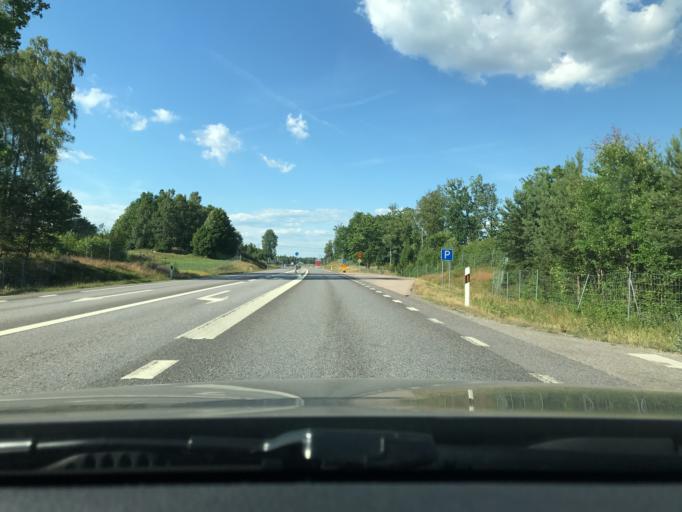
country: SE
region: Kronoberg
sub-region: Almhults Kommun
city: AElmhult
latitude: 56.5224
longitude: 14.1400
